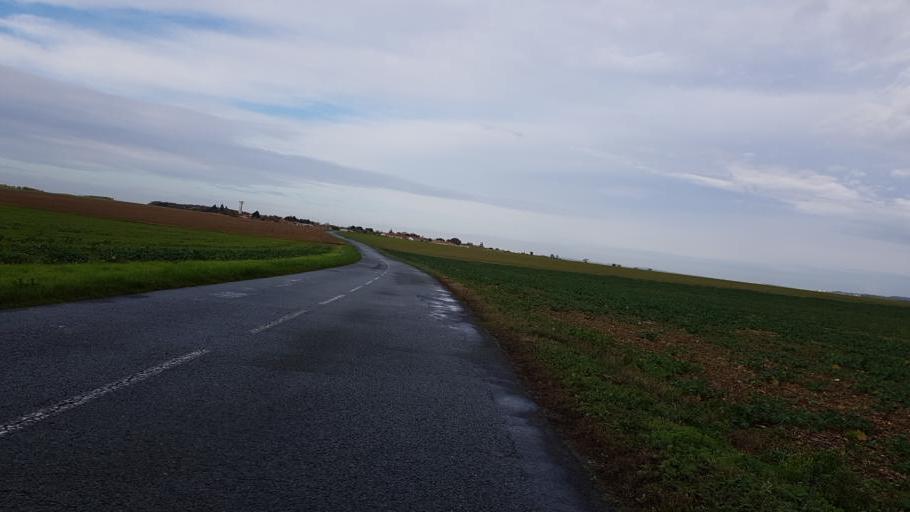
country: FR
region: Poitou-Charentes
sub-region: Departement de la Vienne
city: Chasseneuil-du-Poitou
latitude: 46.6515
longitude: 0.3452
